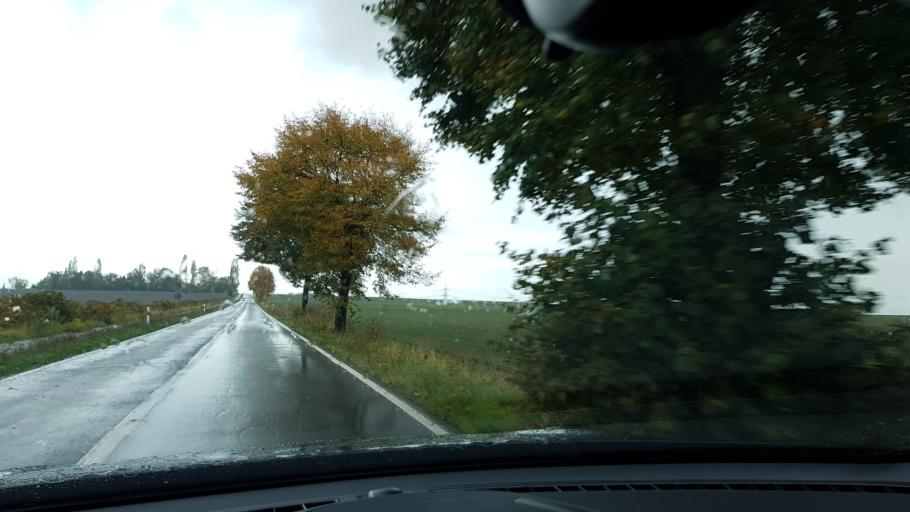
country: DE
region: North Rhine-Westphalia
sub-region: Regierungsbezirk Dusseldorf
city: Rommerskirchen
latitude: 51.0383
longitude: 6.6261
